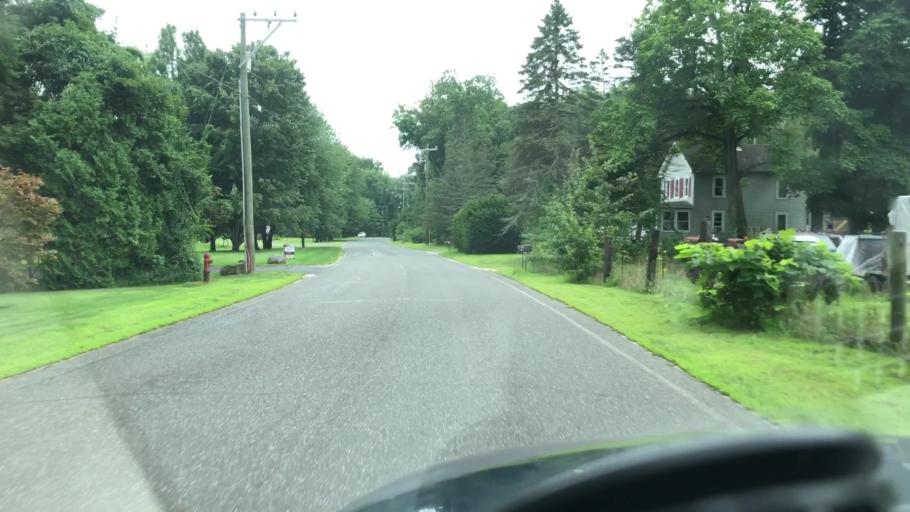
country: US
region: Massachusetts
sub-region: Hampshire County
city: Easthampton
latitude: 42.2434
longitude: -72.6935
